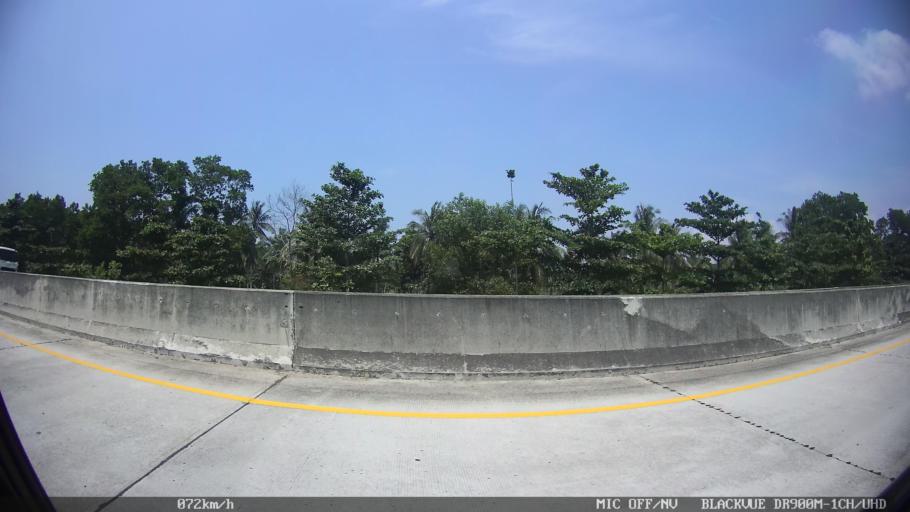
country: ID
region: Lampung
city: Kedaton
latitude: -5.3807
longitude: 105.3330
